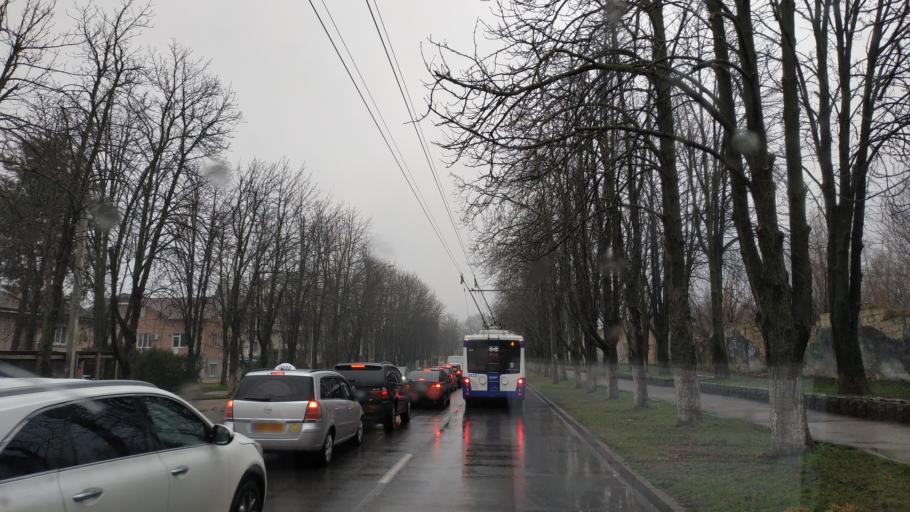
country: MD
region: Chisinau
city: Chisinau
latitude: 47.0238
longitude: 28.8033
